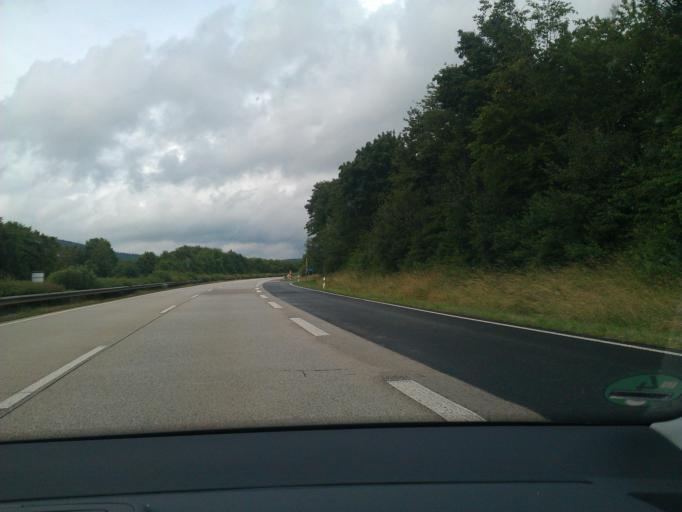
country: DE
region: Rheinland-Pfalz
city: Salmtal
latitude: 49.9179
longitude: 6.8560
